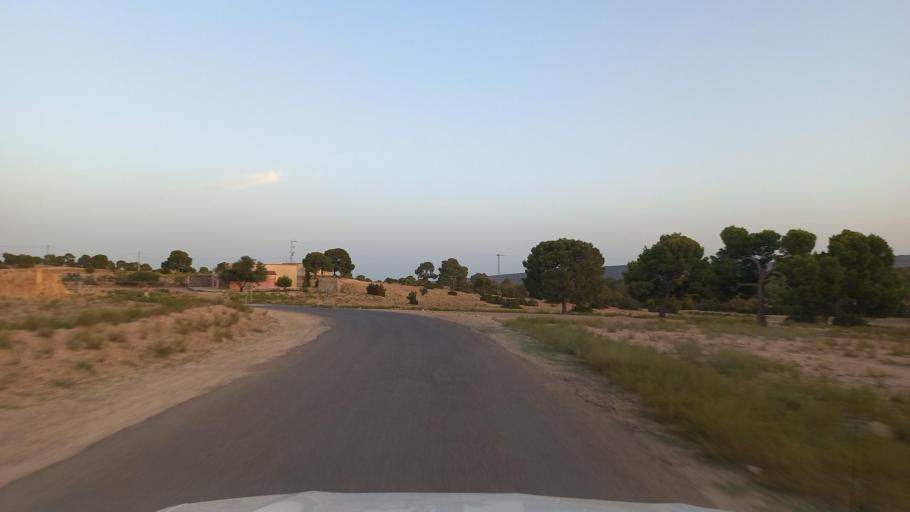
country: TN
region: Al Qasrayn
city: Sbiba
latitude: 35.4143
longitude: 8.9271
